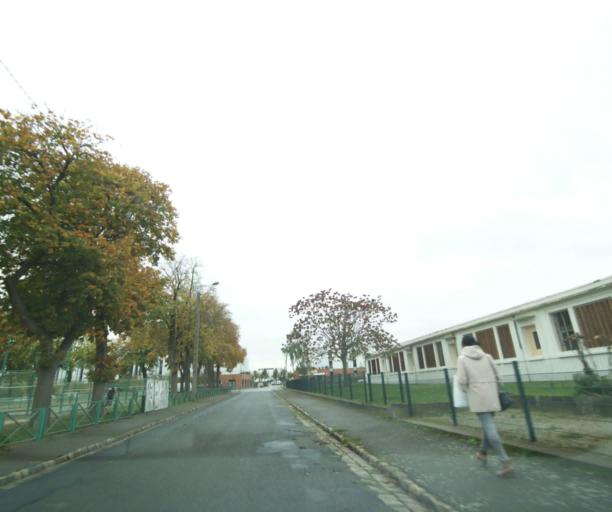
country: FR
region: Centre
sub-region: Departement d'Eure-et-Loir
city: Vernouillet
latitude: 48.7248
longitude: 1.3740
